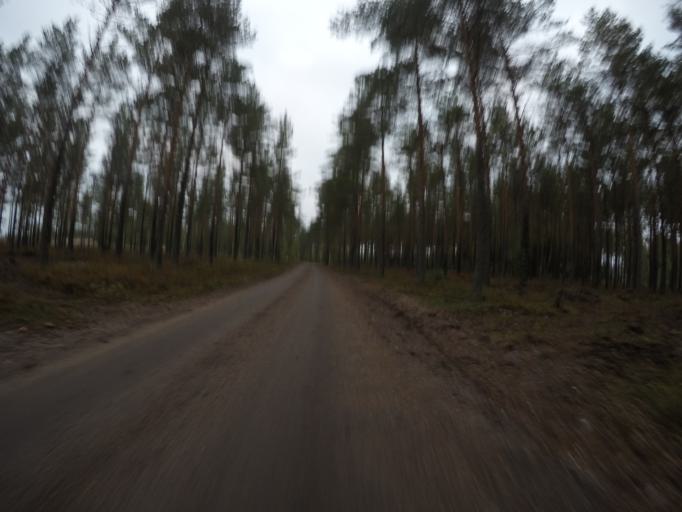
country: SE
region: Vaestmanland
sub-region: Kungsors Kommun
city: Kungsoer
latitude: 59.3780
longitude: 16.1182
